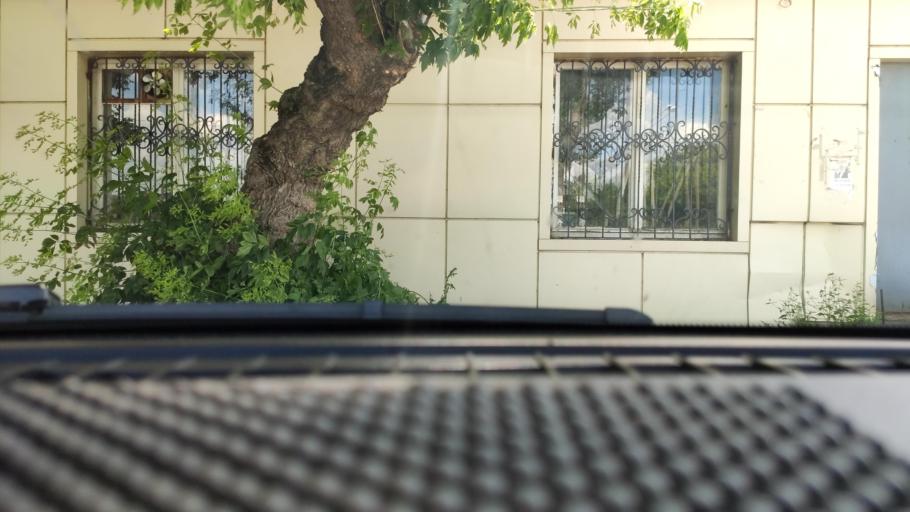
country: RU
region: Voronezj
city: Podkletnoye
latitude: 51.6217
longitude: 39.5587
